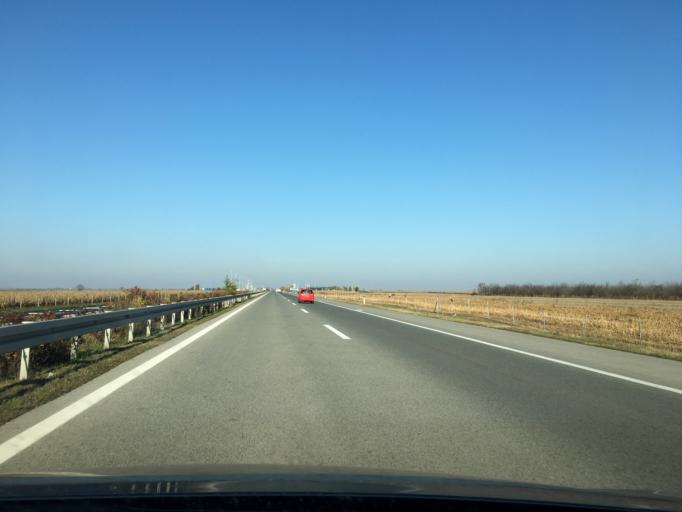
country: RS
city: Rumenka
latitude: 45.3231
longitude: 19.7872
